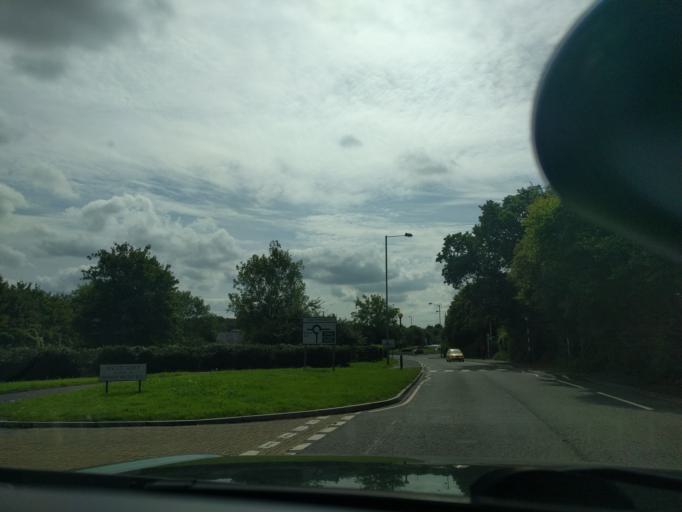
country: GB
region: England
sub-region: Wiltshire
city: Chippenham
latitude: 51.4511
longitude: -2.1393
